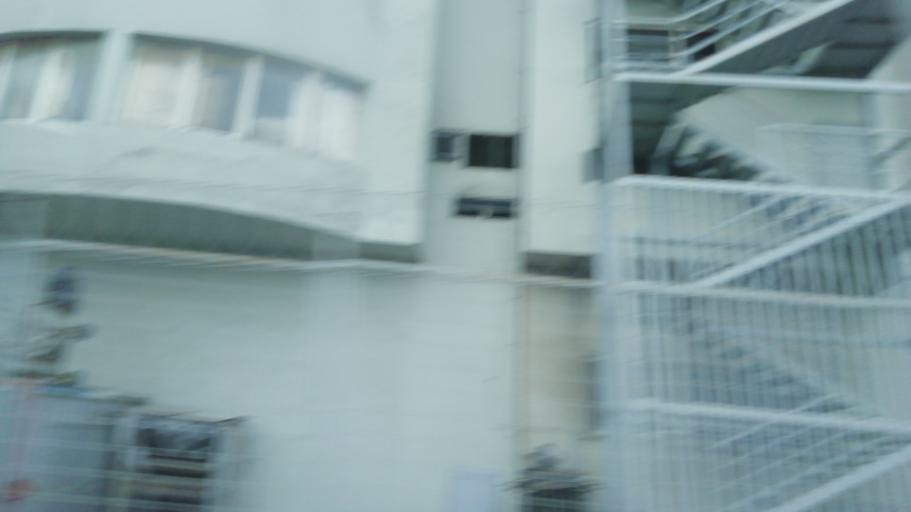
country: TR
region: Istanbul
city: Basaksehir
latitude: 41.0767
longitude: 28.8131
